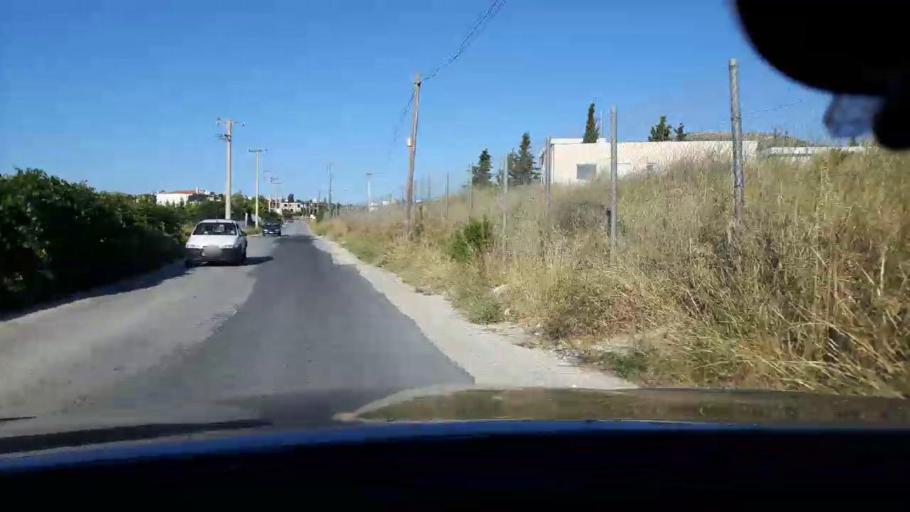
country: GR
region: Attica
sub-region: Nomarchia Anatolikis Attikis
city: Limin Mesoyaias
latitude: 37.8870
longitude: 23.9759
